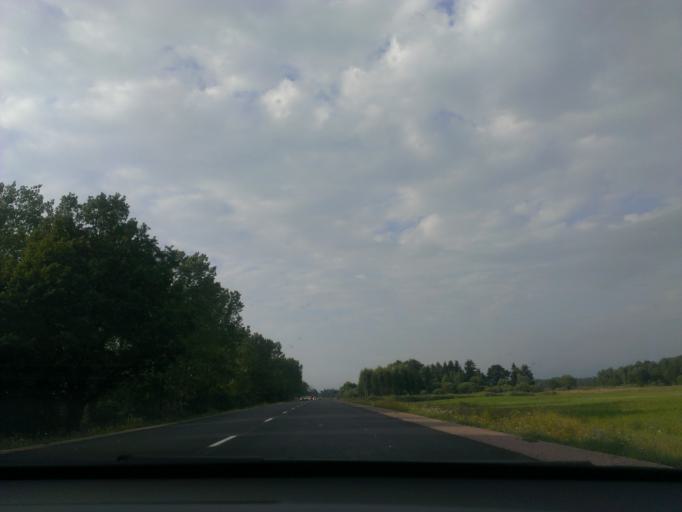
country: LV
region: Lecava
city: Iecava
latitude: 56.6776
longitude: 24.2372
